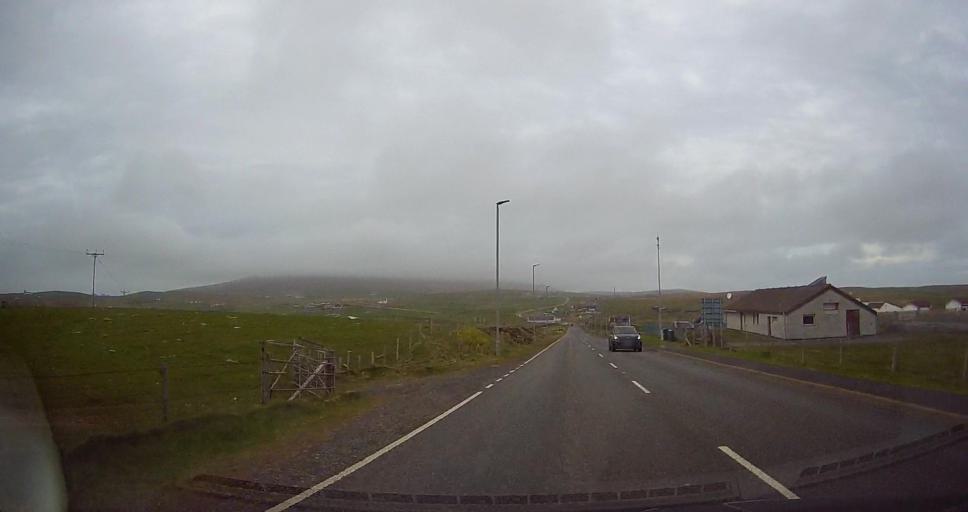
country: GB
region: Scotland
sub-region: Shetland Islands
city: Sandwick
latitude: 59.9208
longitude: -1.2988
